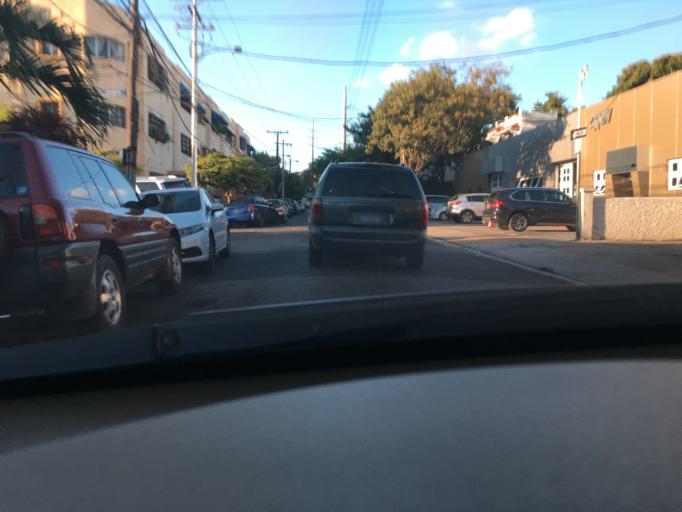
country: DO
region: Nacional
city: Ciudad Nueva
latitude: 18.4707
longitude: -69.9012
